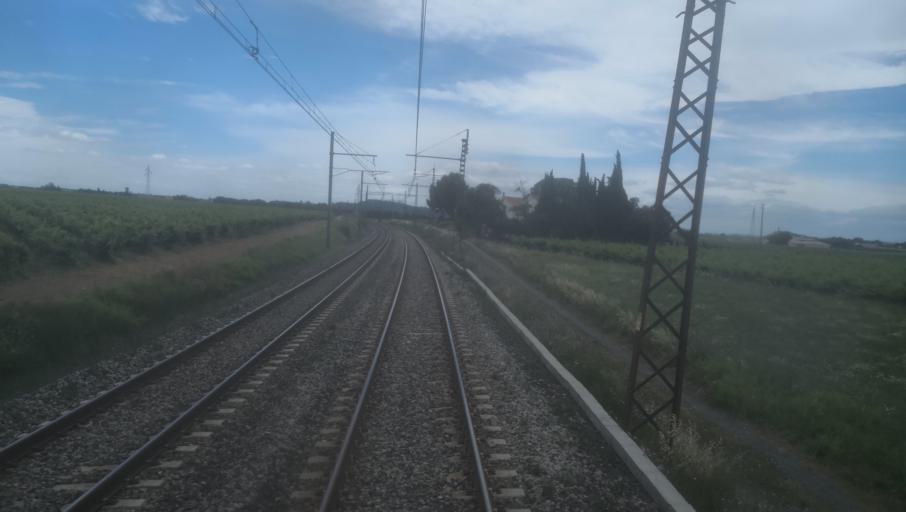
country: FR
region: Languedoc-Roussillon
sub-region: Departement de l'Herault
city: Colombiers
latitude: 43.3303
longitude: 3.1613
